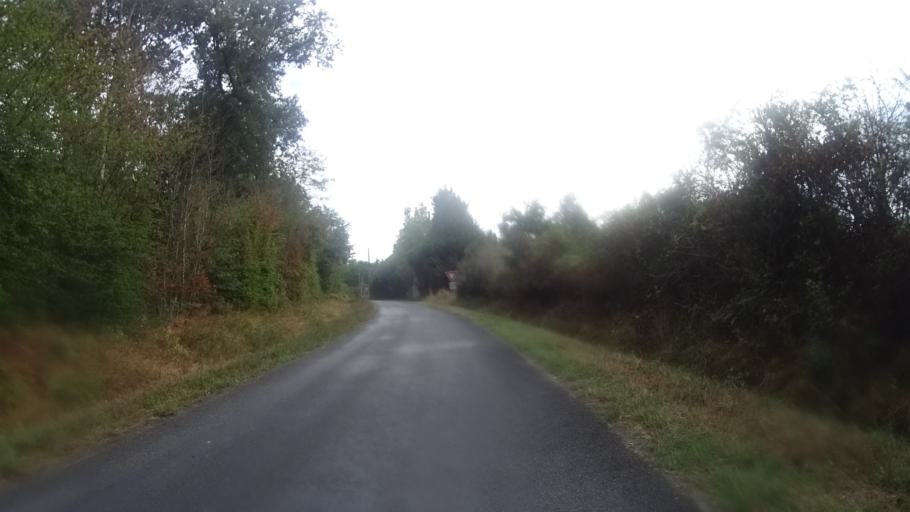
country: FR
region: Centre
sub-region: Departement du Loiret
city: Fay-aux-Loges
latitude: 47.9283
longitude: 2.1956
